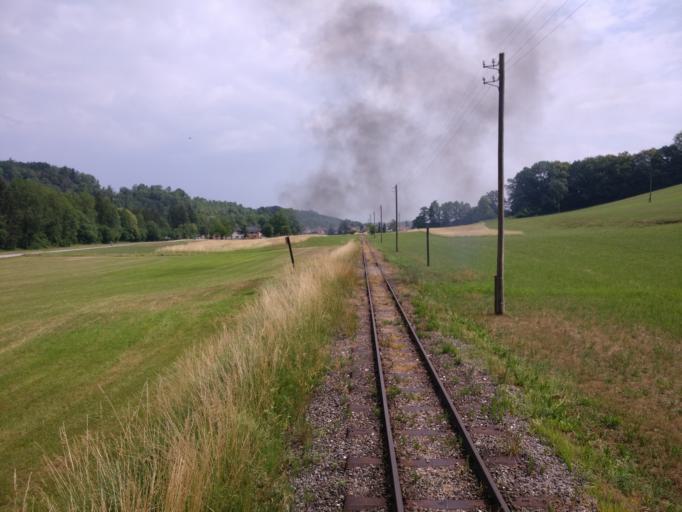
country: AT
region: Upper Austria
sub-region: Politischer Bezirk Steyr-Land
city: Sierning
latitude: 48.0114
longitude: 14.3098
